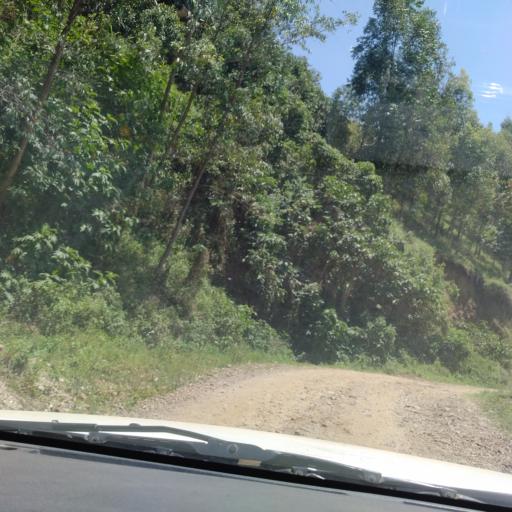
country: CD
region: Nord Kivu
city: Sake
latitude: -1.9734
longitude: 28.9140
